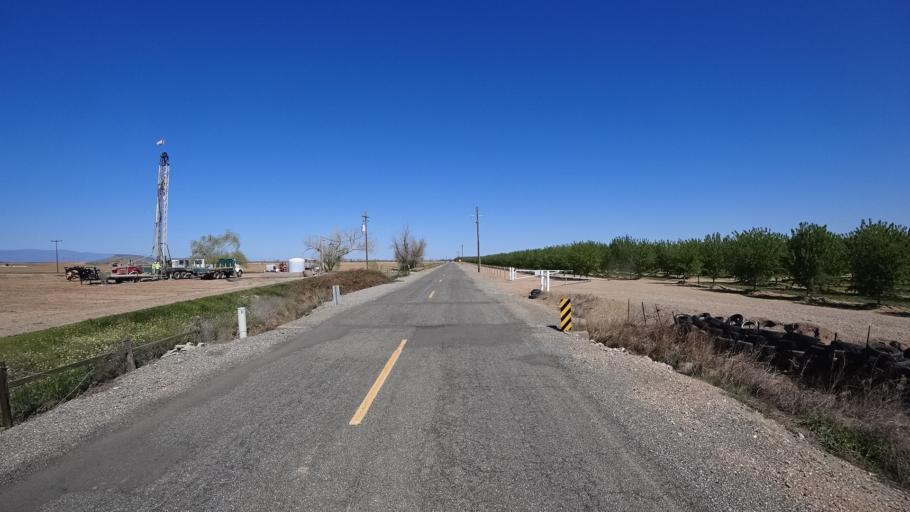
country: US
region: California
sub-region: Glenn County
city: Orland
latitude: 39.6932
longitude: -122.2530
